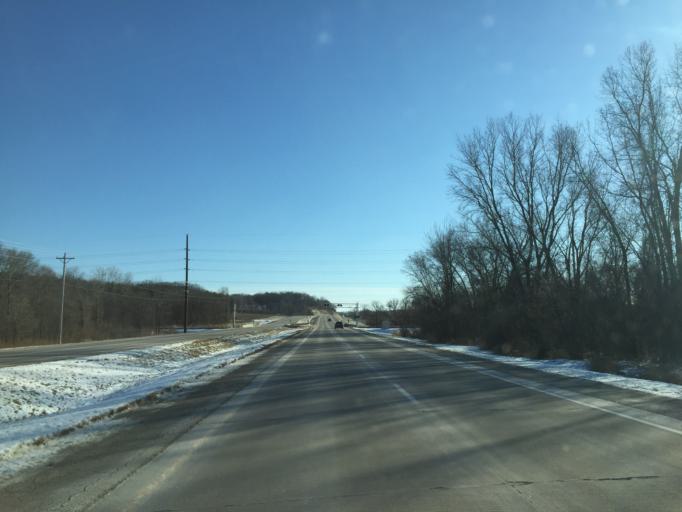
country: US
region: Minnesota
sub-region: Olmsted County
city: Rochester
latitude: 44.0306
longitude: -92.4234
